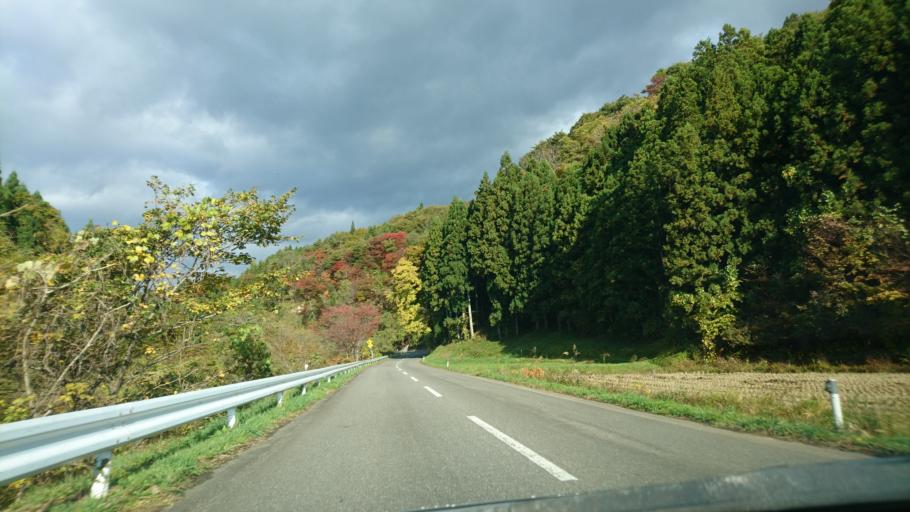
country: JP
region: Iwate
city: Mizusawa
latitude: 39.0826
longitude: 140.9979
